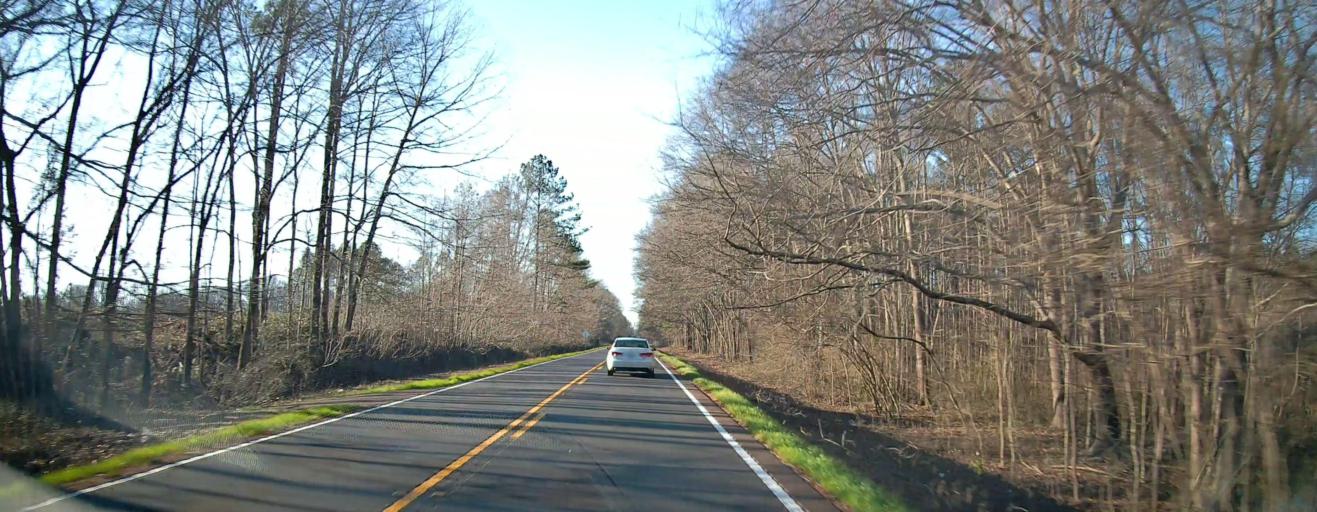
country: US
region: Georgia
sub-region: Harris County
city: Pine Mountain
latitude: 32.9172
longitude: -84.7636
